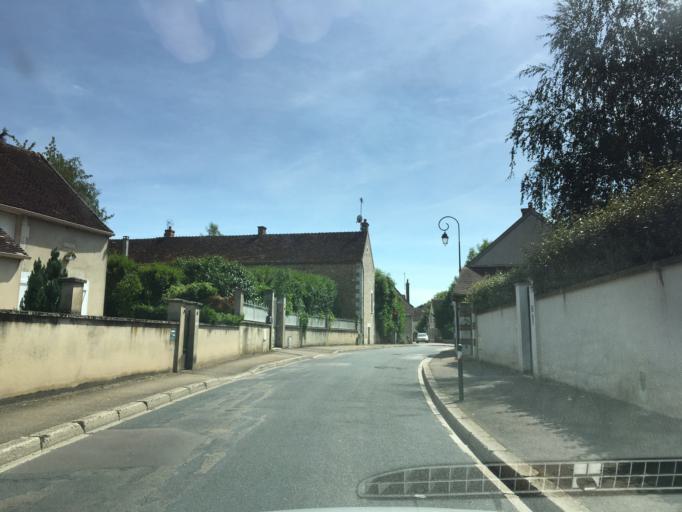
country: FR
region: Bourgogne
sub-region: Departement de l'Yonne
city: Saint-Georges-sur-Baulche
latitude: 47.8068
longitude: 3.5339
